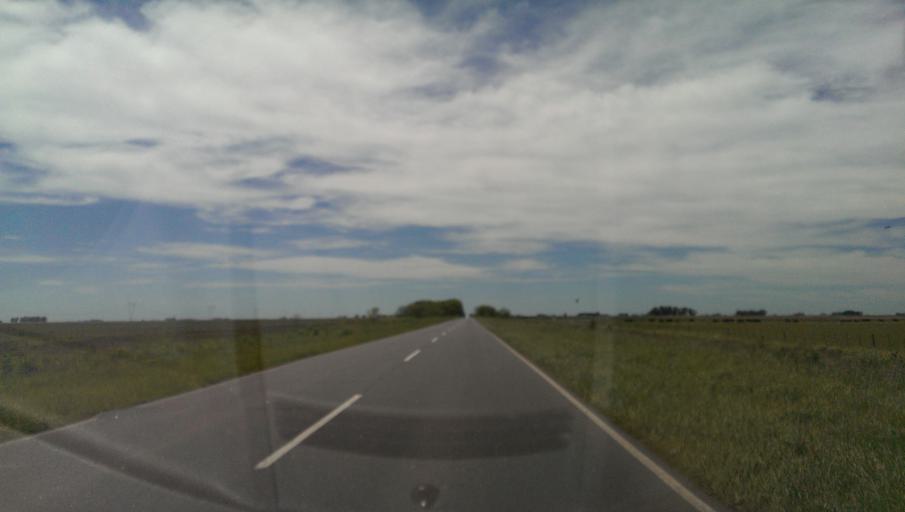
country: AR
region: Buenos Aires
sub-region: Partido de Laprida
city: Laprida
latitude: -37.2190
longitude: -60.6938
